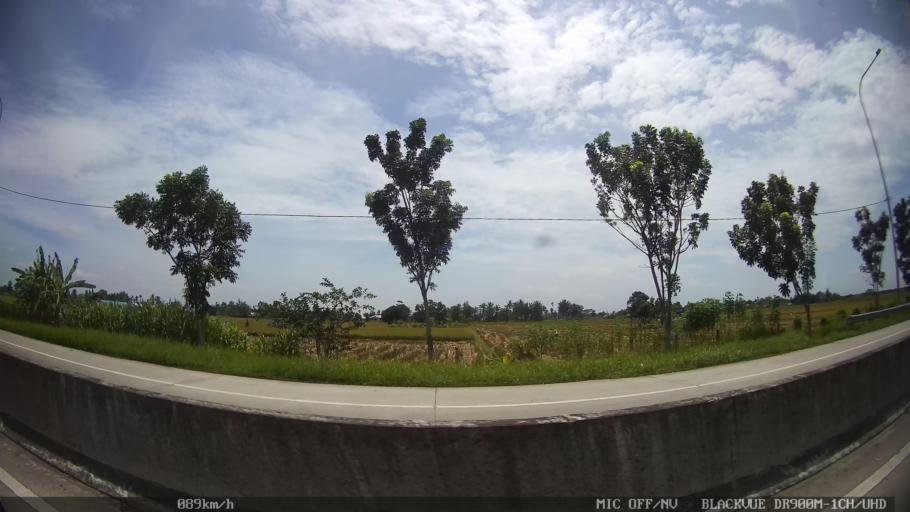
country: ID
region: North Sumatra
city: Perbaungan
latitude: 3.5476
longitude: 98.8897
